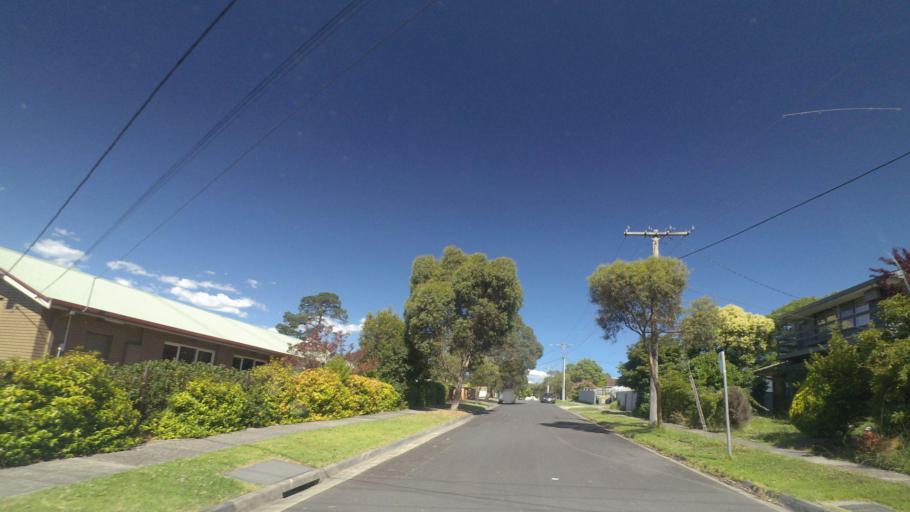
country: AU
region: Victoria
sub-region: Knox
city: Bayswater
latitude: -37.8599
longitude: 145.2589
